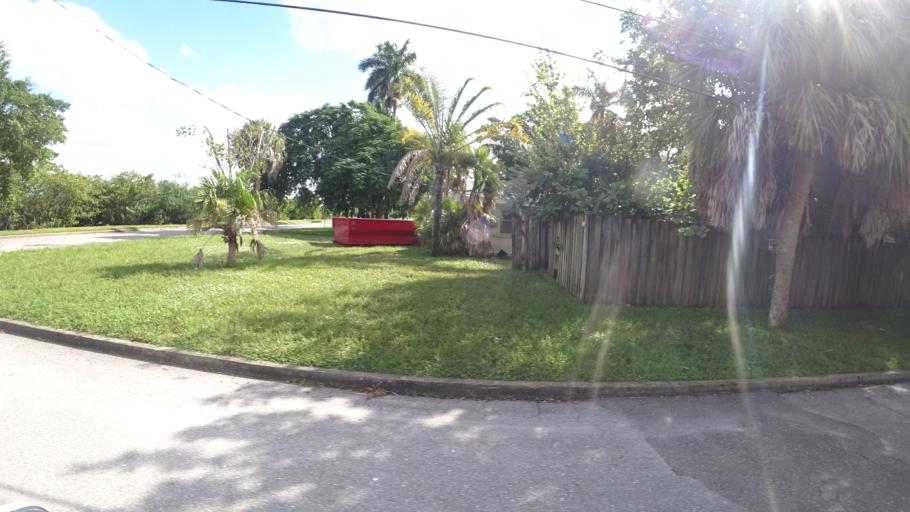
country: US
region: Florida
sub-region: Manatee County
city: Bradenton
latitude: 27.4979
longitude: -82.5547
